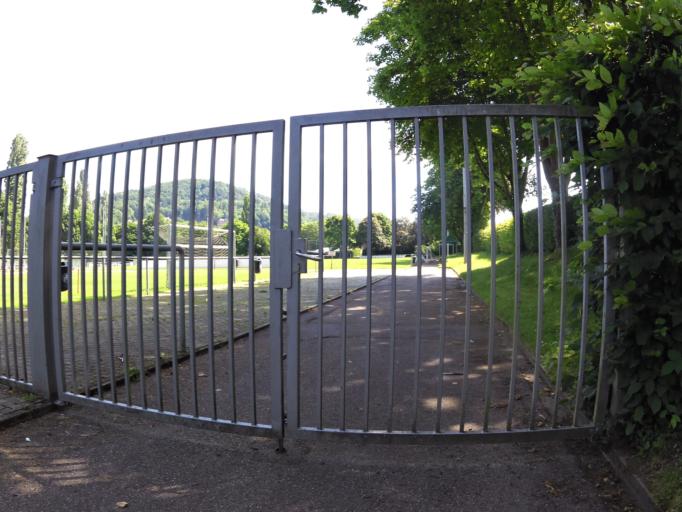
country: DE
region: Baden-Wuerttemberg
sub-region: Freiburg Region
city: Lahr
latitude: 48.3383
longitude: 7.8813
